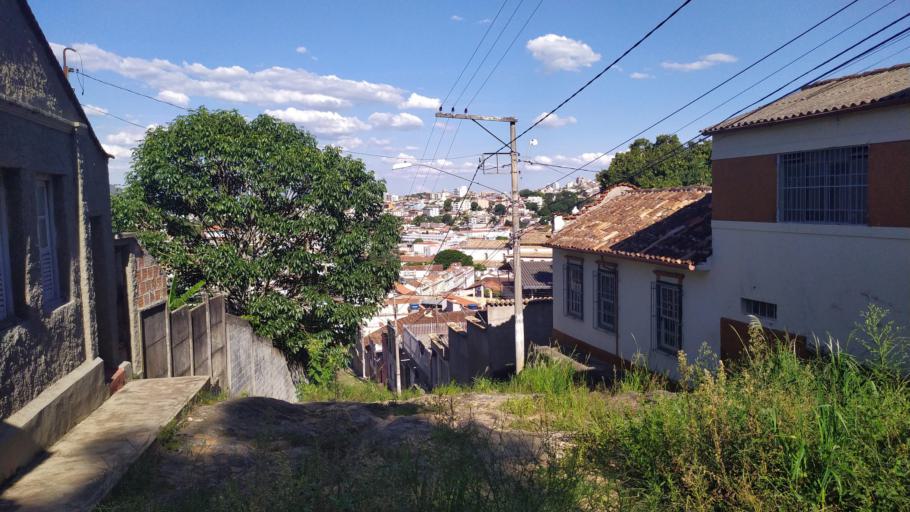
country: BR
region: Minas Gerais
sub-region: Sao Joao Del Rei
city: Sao Joao del Rei
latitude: -21.1328
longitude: -44.2634
